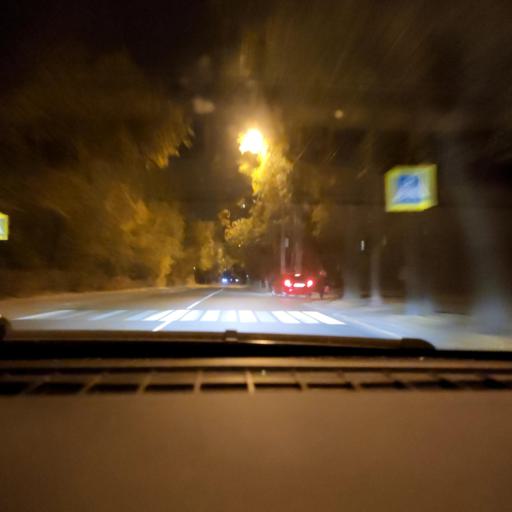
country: RU
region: Voronezj
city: Voronezh
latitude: 51.6924
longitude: 39.2620
